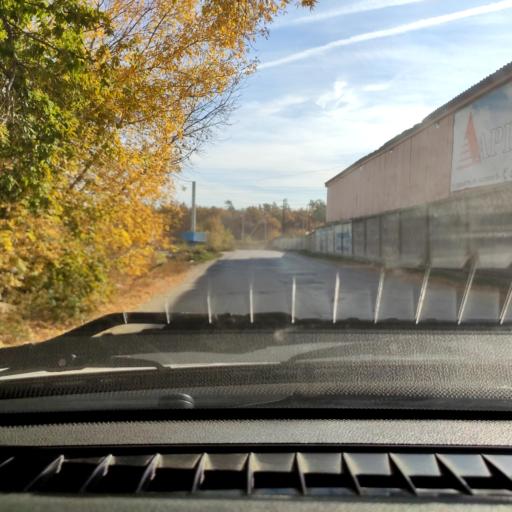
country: RU
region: Samara
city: Zhigulevsk
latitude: 53.5217
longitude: 49.4844
